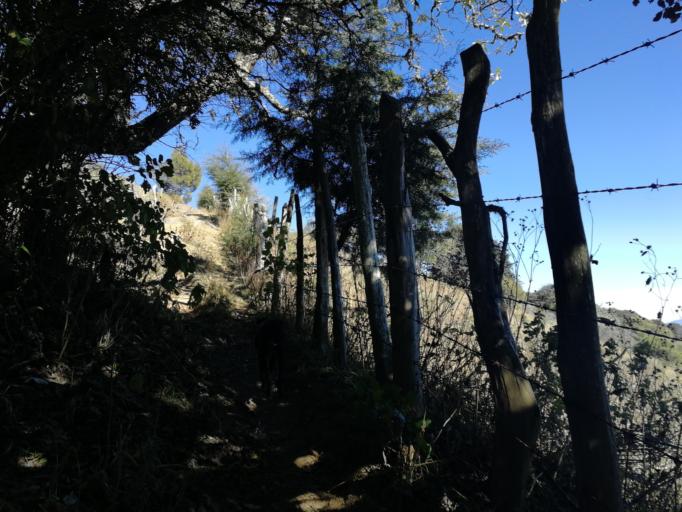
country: MX
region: San Luis Potosi
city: Zaragoza
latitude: 22.0069
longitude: -100.6092
